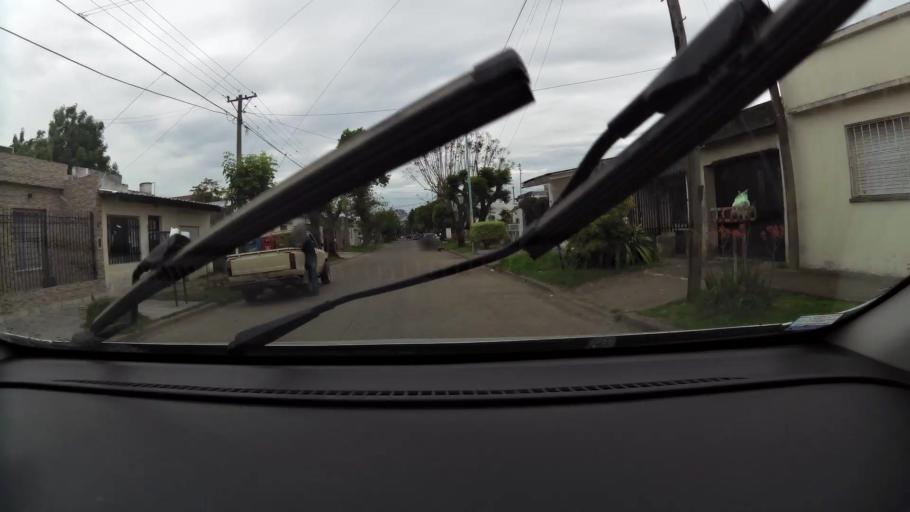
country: AR
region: Buenos Aires
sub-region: Partido de Zarate
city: Zarate
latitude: -34.0923
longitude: -59.0330
